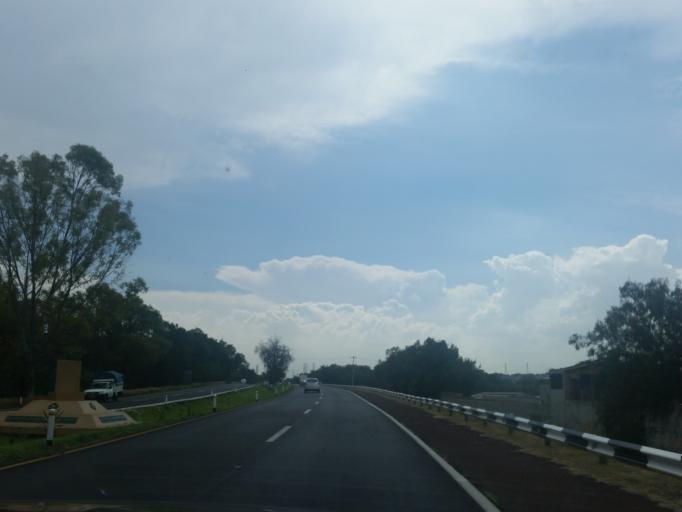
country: MX
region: Mexico
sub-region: Acolman de Nezahualcoyotl
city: Prados de San Juan
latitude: 19.6207
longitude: -98.9603
